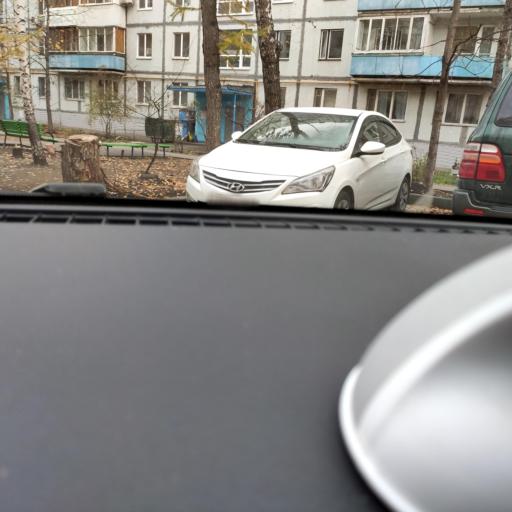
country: RU
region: Samara
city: Samara
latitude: 53.2435
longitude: 50.2553
